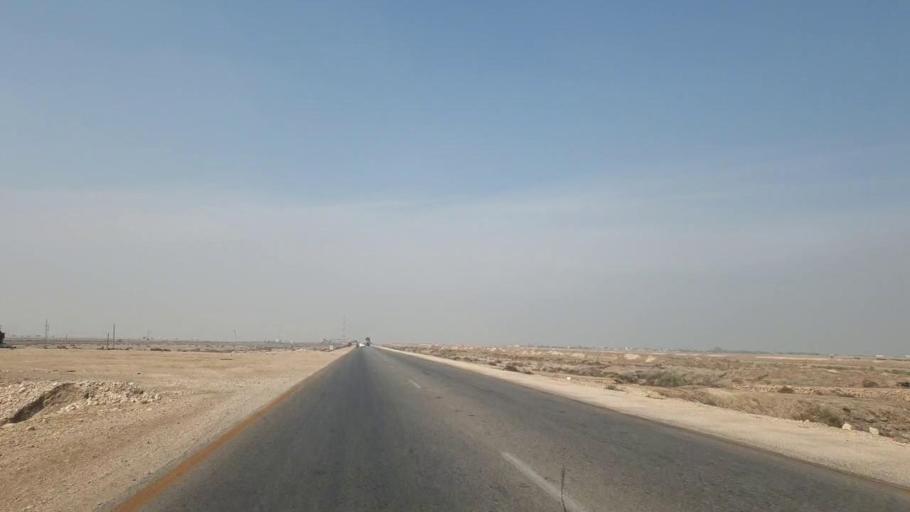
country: PK
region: Sindh
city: Sann
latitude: 25.8908
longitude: 68.2401
